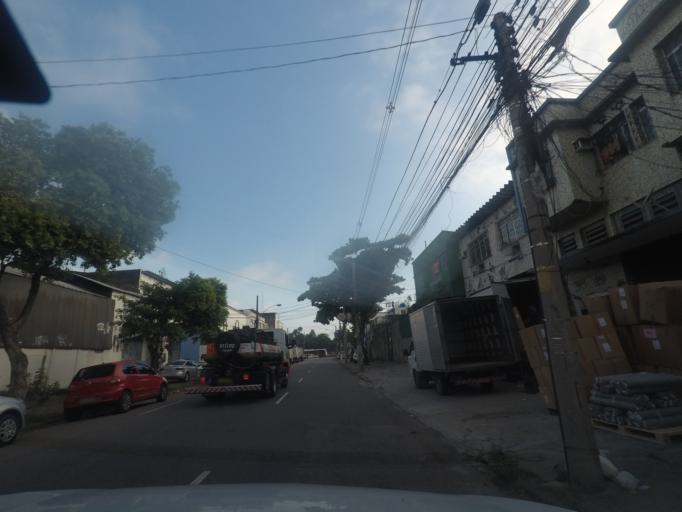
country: BR
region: Rio de Janeiro
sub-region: Duque De Caxias
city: Duque de Caxias
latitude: -22.8291
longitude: -43.2741
